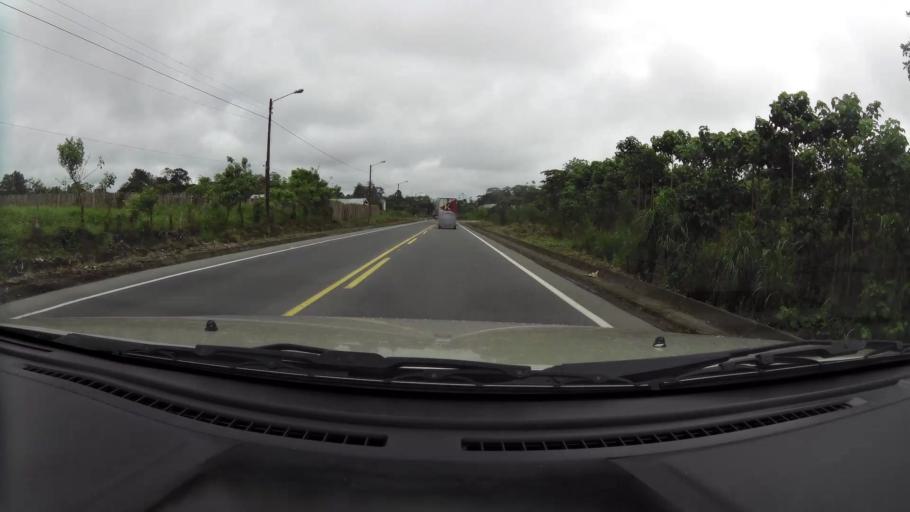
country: EC
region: Santo Domingo de los Tsachilas
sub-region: Canton Santo Domingo de los Colorados
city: Santo Domingo de los Colorados
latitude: -0.2626
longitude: -79.1352
